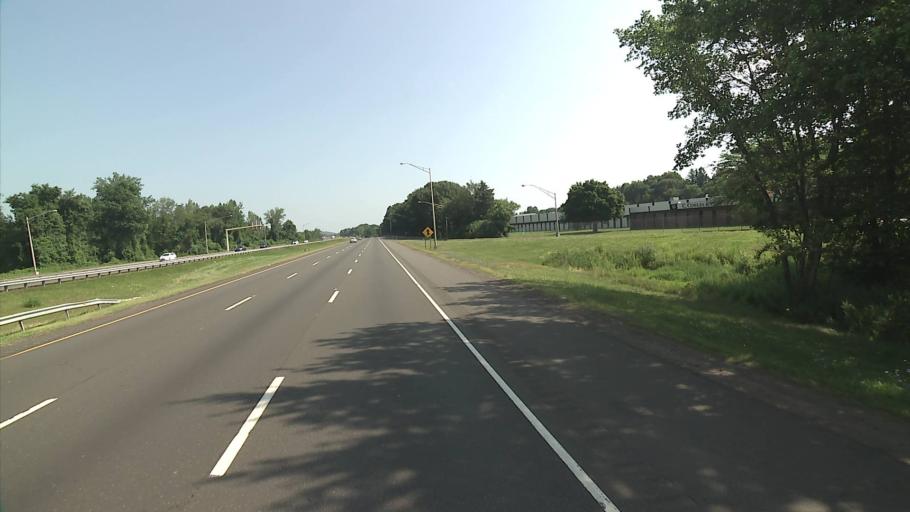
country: US
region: Connecticut
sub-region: New Haven County
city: North Haven
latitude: 41.3786
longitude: -72.8680
